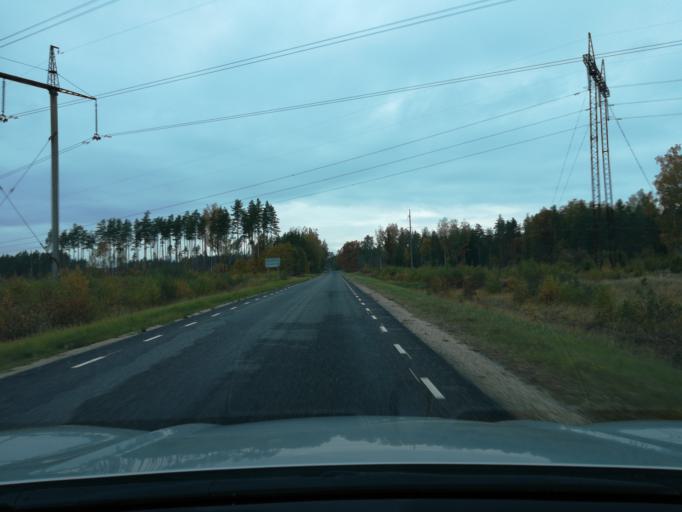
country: EE
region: Ida-Virumaa
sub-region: Johvi vald
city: Johvi
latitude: 59.0171
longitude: 27.4105
